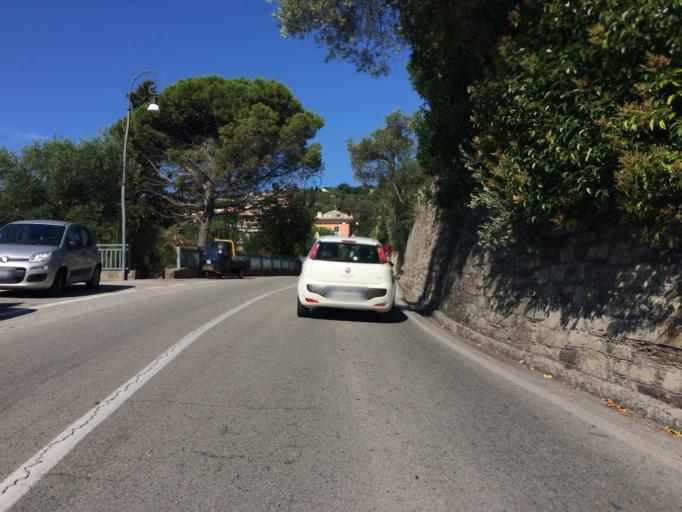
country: IT
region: Liguria
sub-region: Provincia di Genova
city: Rapallo
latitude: 44.3448
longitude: 9.2181
